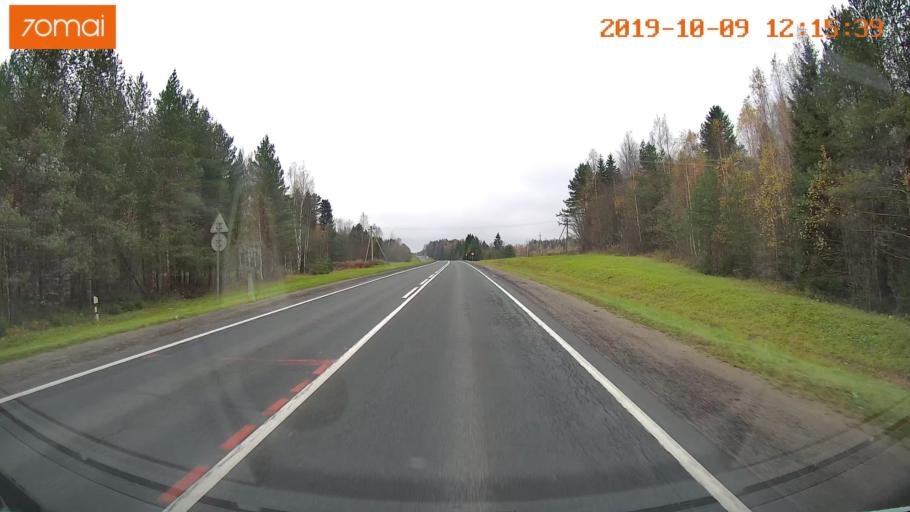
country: RU
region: Jaroslavl
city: Prechistoye
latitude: 58.4802
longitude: 40.3230
